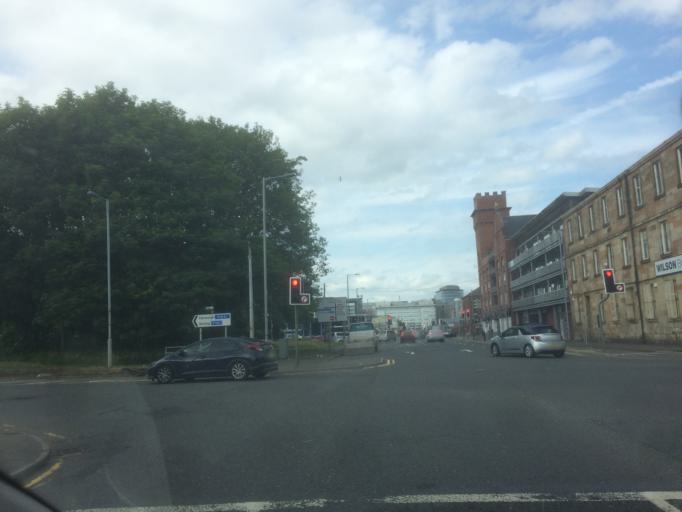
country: GB
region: Scotland
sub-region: Glasgow City
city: Glasgow
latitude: 55.8513
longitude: -4.2655
